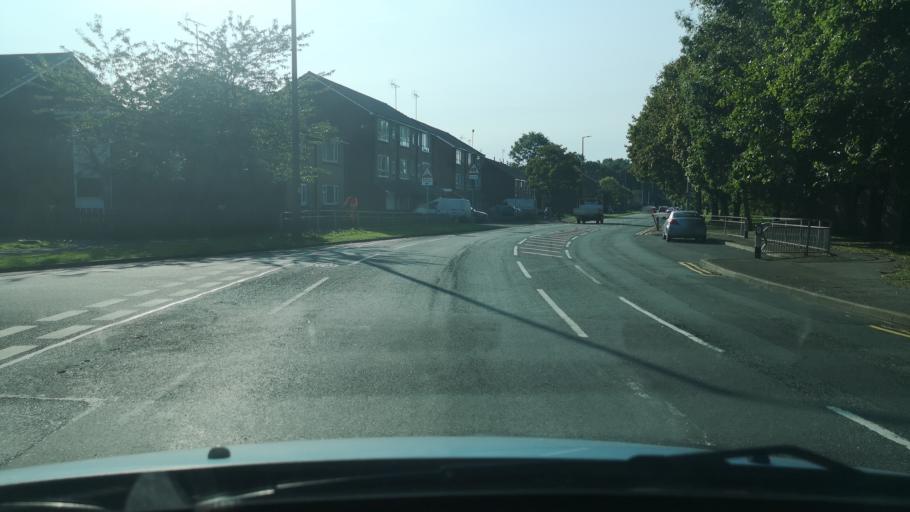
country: GB
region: England
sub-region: North Lincolnshire
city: Scunthorpe
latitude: 53.5742
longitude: -0.6776
